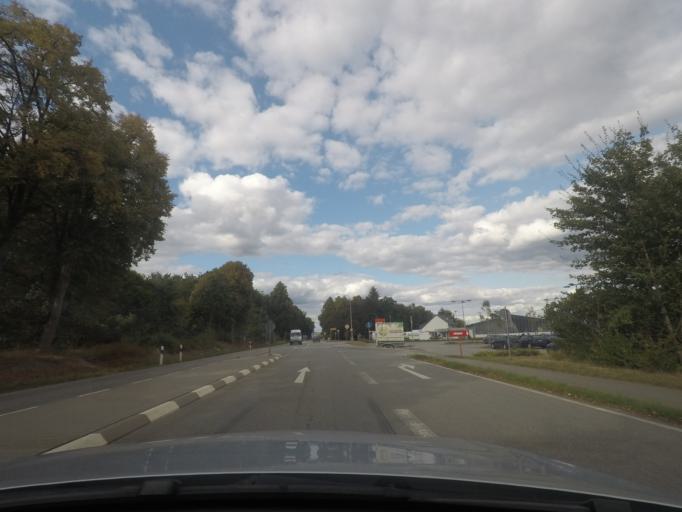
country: DE
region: Rheinland-Pfalz
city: Mehlingen
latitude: 49.4851
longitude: 7.8455
